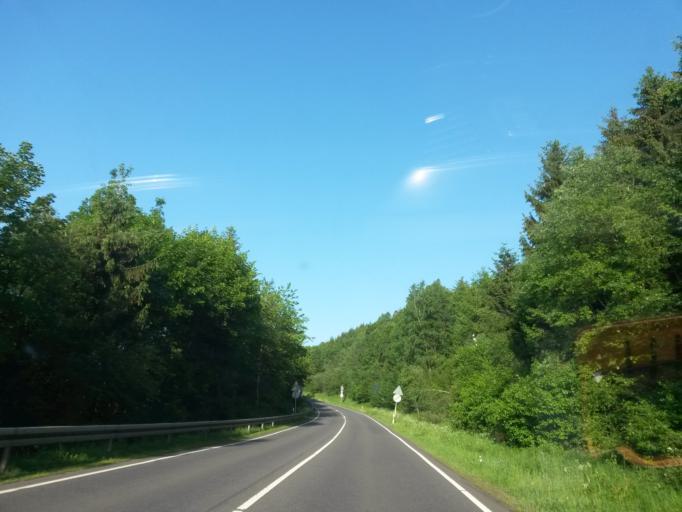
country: DE
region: North Rhine-Westphalia
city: Bergneustadt
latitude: 51.0103
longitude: 7.6357
